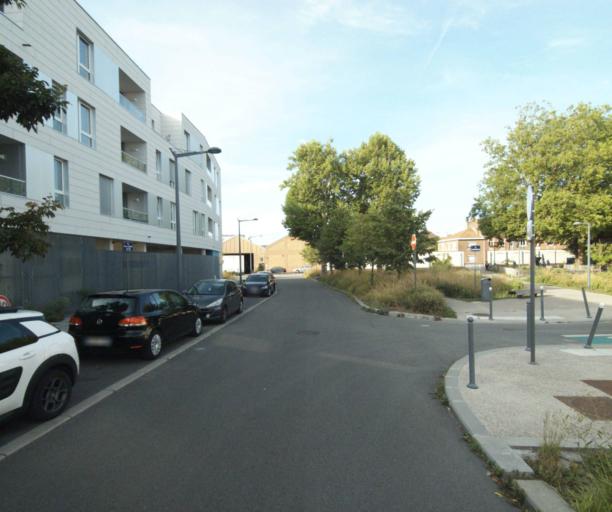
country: FR
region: Nord-Pas-de-Calais
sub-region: Departement du Nord
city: Lille
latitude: 50.6115
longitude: 3.0676
